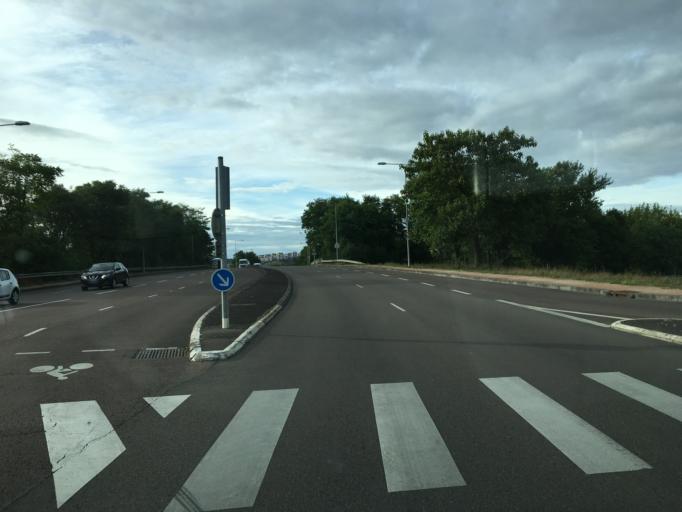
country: FR
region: Bourgogne
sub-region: Departement de la Cote-d'Or
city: Dijon
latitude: 47.3161
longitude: 5.0130
